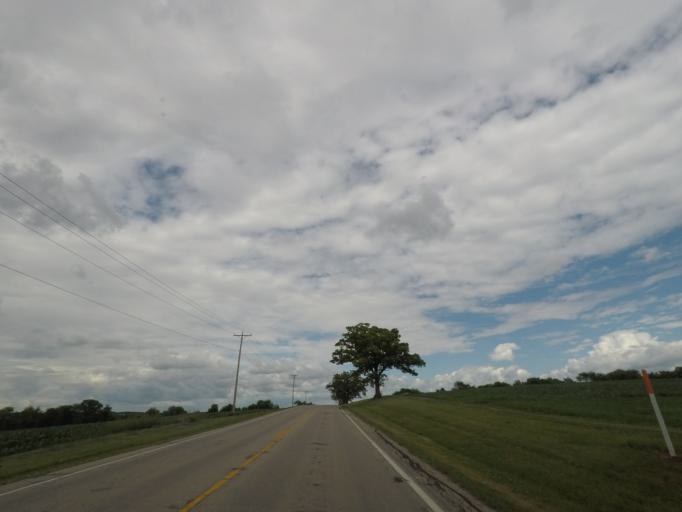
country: US
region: Wisconsin
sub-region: Green County
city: Brooklyn
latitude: 42.8481
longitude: -89.3976
